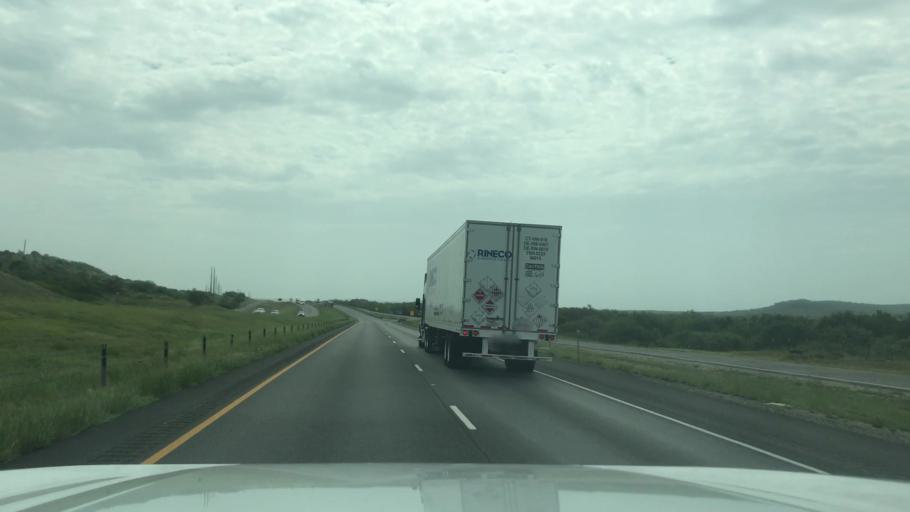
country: US
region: Texas
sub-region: Callahan County
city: Baird
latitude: 32.3927
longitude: -99.3524
